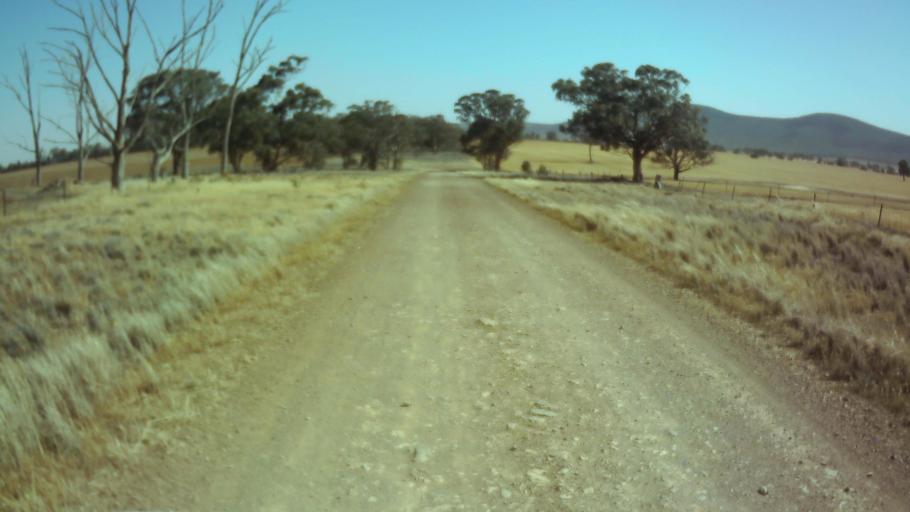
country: AU
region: New South Wales
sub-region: Weddin
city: Grenfell
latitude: -33.8540
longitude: 148.0159
